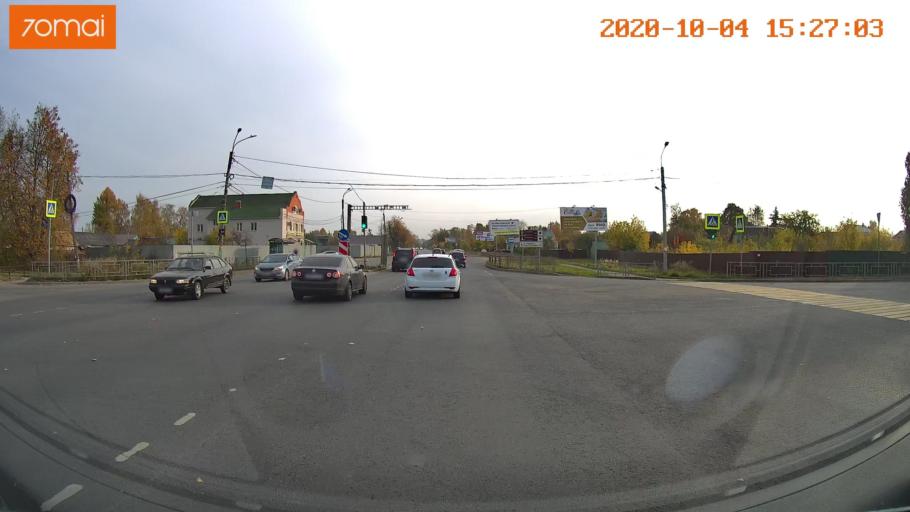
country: RU
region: Ivanovo
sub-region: Gorod Ivanovo
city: Ivanovo
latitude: 57.0429
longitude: 40.9671
